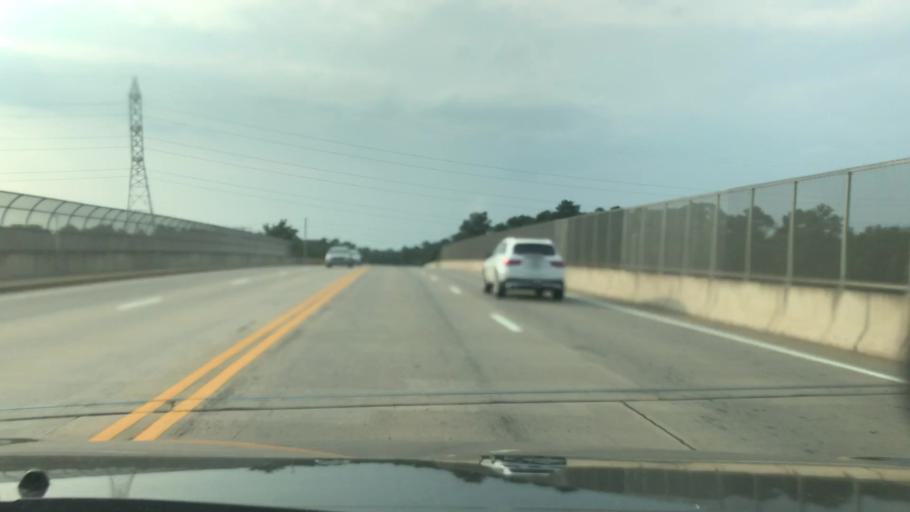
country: US
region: New Jersey
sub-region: Ocean County
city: Leisure Village
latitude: 40.0654
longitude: -74.1617
